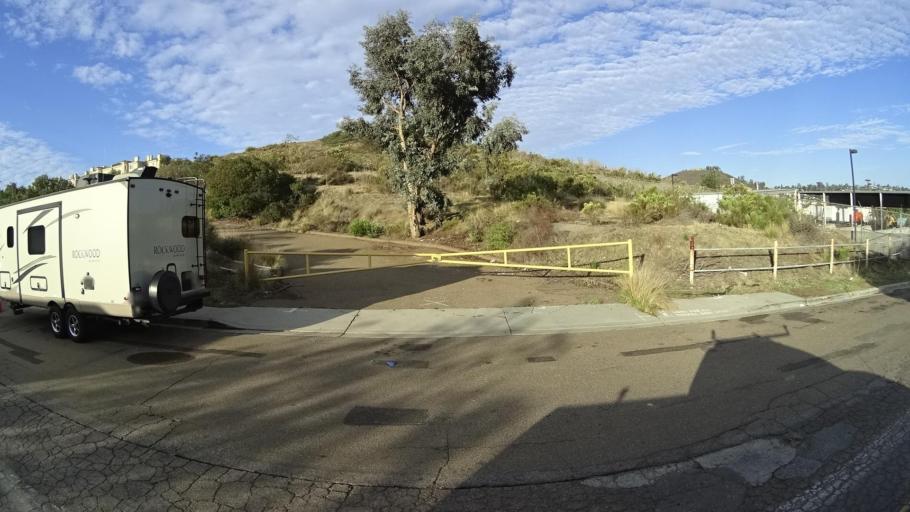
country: US
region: California
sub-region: San Diego County
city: La Presa
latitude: 32.7231
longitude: -116.9662
